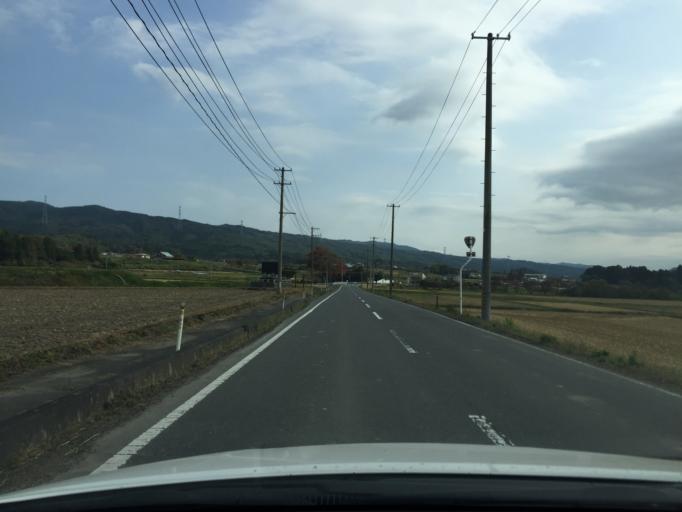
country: JP
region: Fukushima
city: Ishikawa
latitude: 36.9753
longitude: 140.4291
